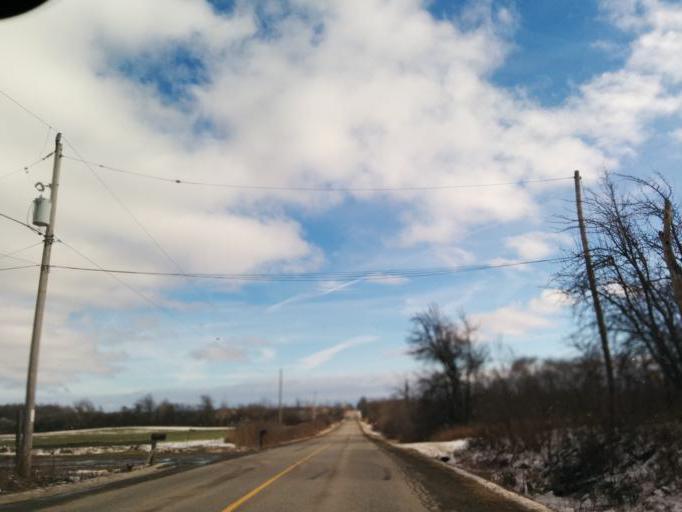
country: CA
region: Ontario
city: Brantford
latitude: 42.9918
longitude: -80.0770
